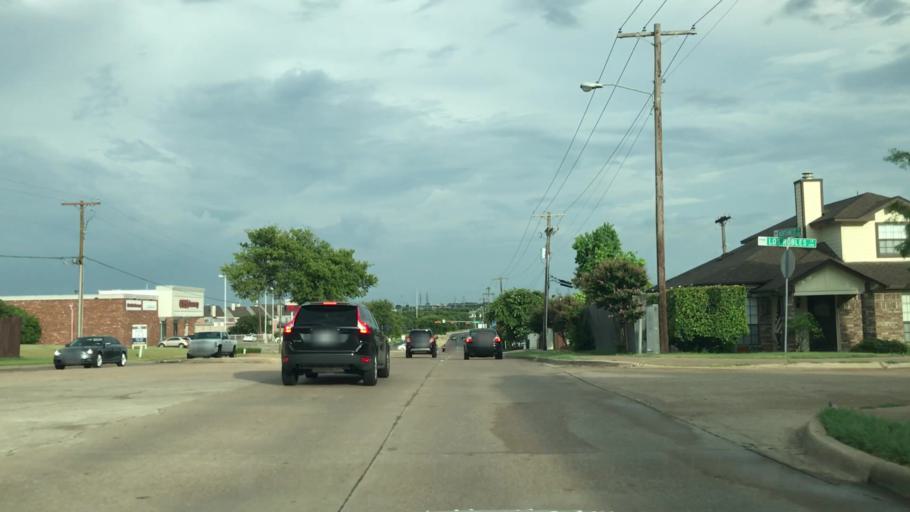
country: US
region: Texas
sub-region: Dallas County
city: Garland
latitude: 32.8427
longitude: -96.6261
